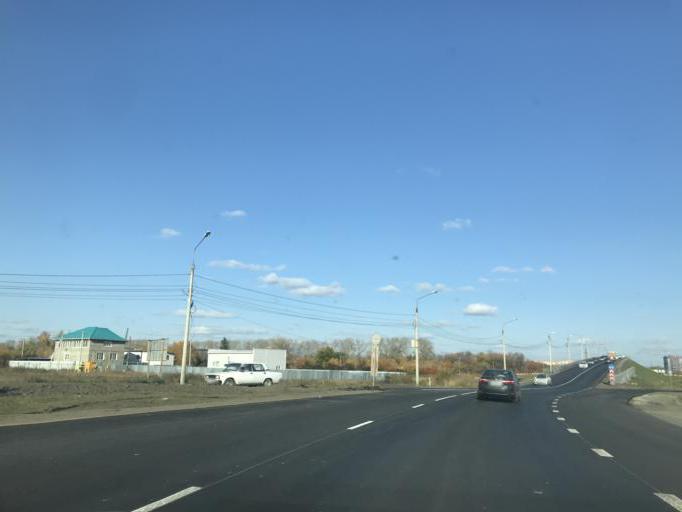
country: RU
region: Chelyabinsk
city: Roshchino
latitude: 55.2306
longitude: 61.2876
